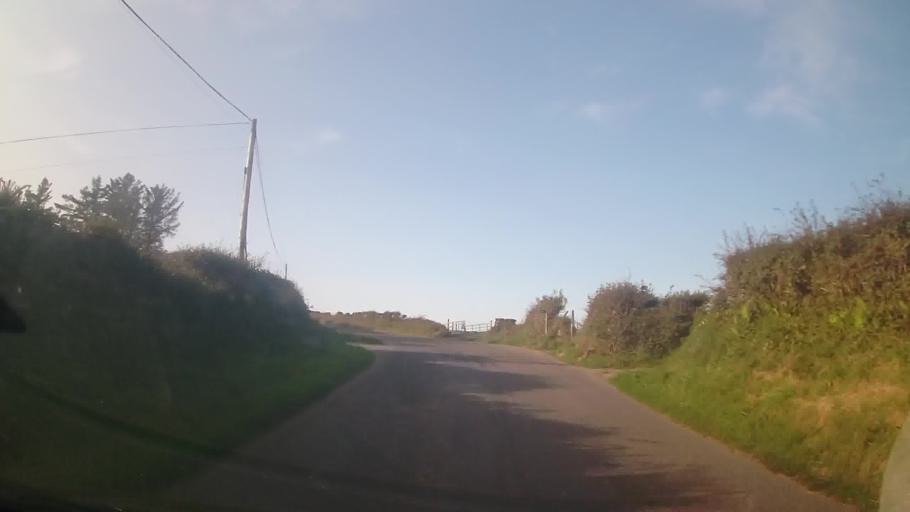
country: GB
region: Wales
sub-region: Pembrokeshire
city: Fishguard
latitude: 51.9848
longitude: -4.9561
